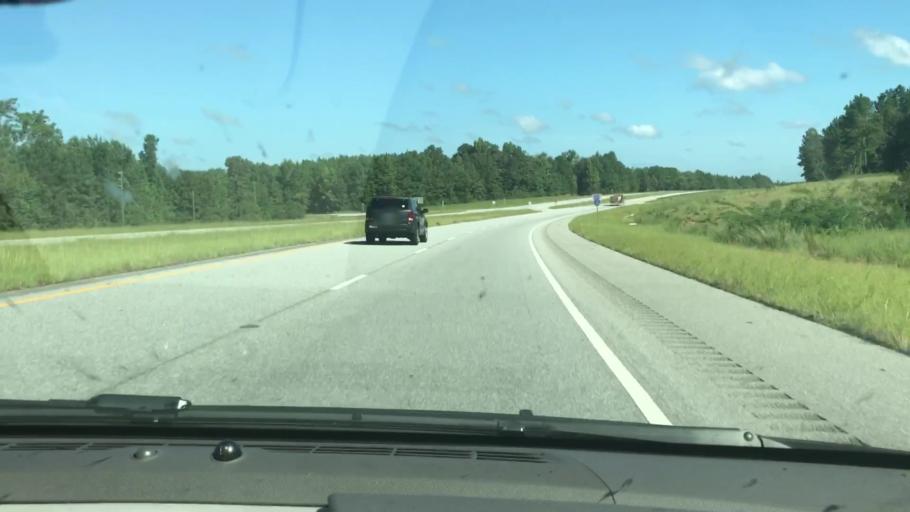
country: US
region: Alabama
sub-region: Barbour County
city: Eufaula
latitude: 32.1553
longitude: -85.1777
